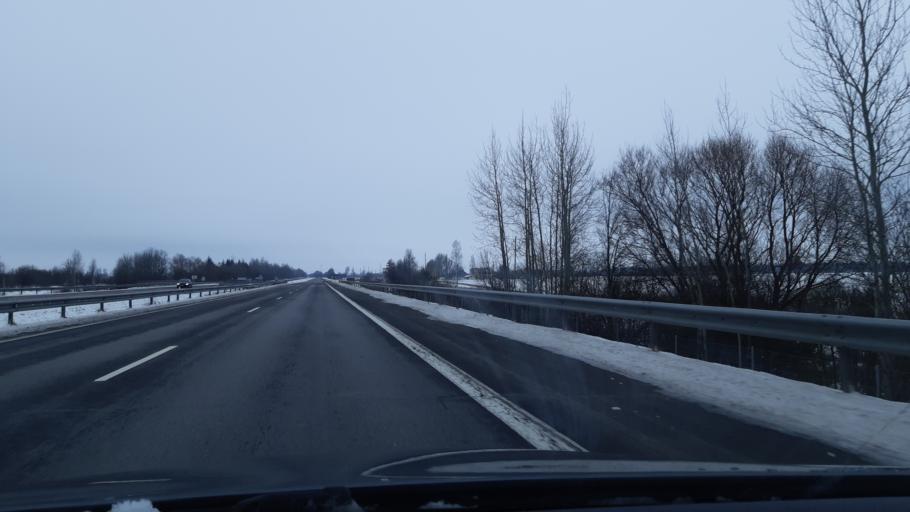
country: LT
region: Kauno apskritis
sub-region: Kaunas
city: Sargenai
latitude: 55.0689
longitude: 23.8157
